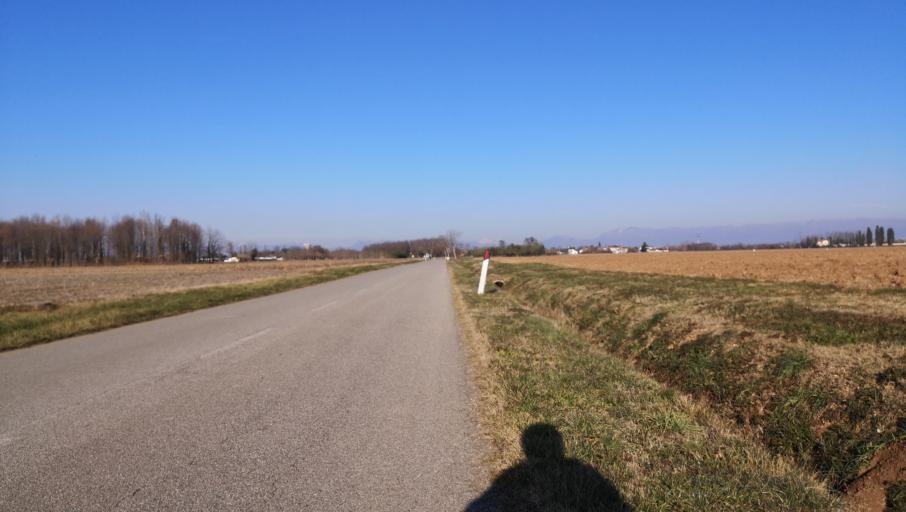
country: IT
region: Friuli Venezia Giulia
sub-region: Provincia di Udine
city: Santa Maria la Longa
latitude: 45.9462
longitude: 13.2745
